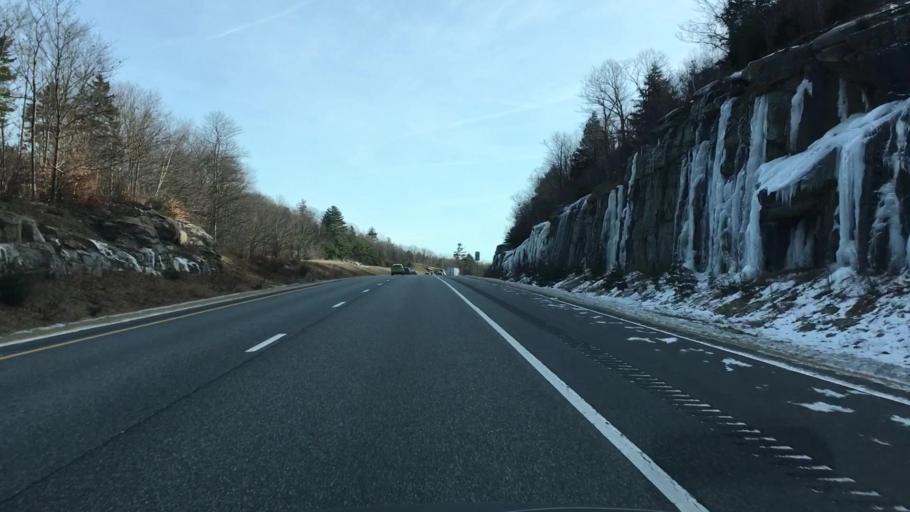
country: US
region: New Hampshire
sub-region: Sullivan County
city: Grantham
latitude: 43.4638
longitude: -72.0993
